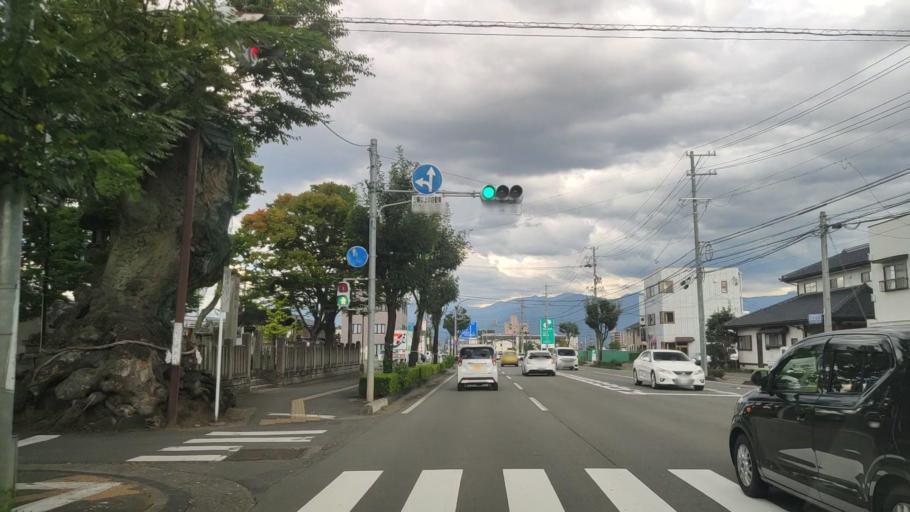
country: JP
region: Nagano
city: Nagano-shi
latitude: 36.6539
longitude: 138.2123
